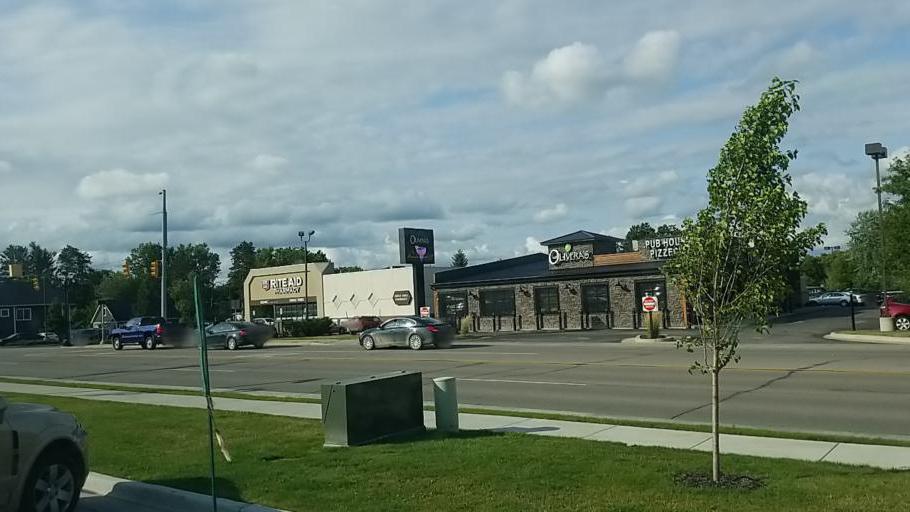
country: US
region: Michigan
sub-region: Ionia County
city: Portland
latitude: 42.8637
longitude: -84.8889
